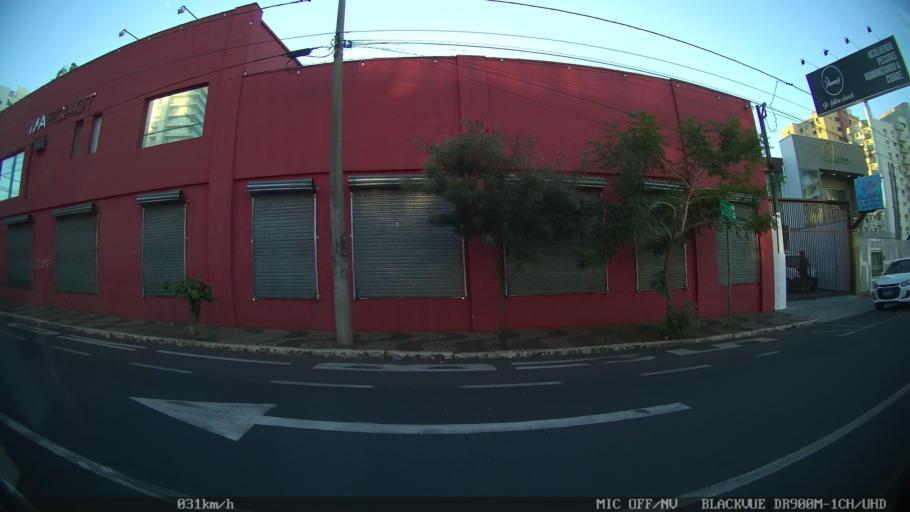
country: BR
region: Sao Paulo
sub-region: Sao Jose Do Rio Preto
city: Sao Jose do Rio Preto
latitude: -20.8122
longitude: -49.3763
